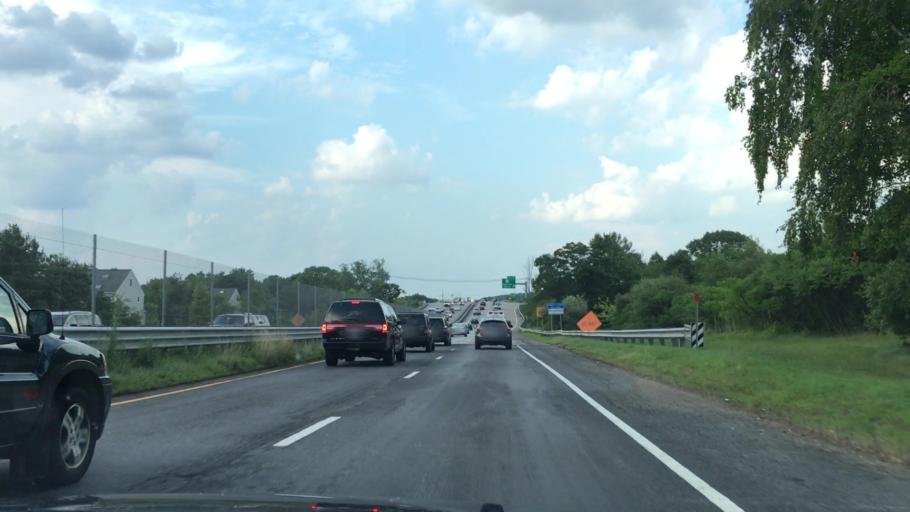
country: US
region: Massachusetts
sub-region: Essex County
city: Danvers
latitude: 42.5548
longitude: -70.9328
